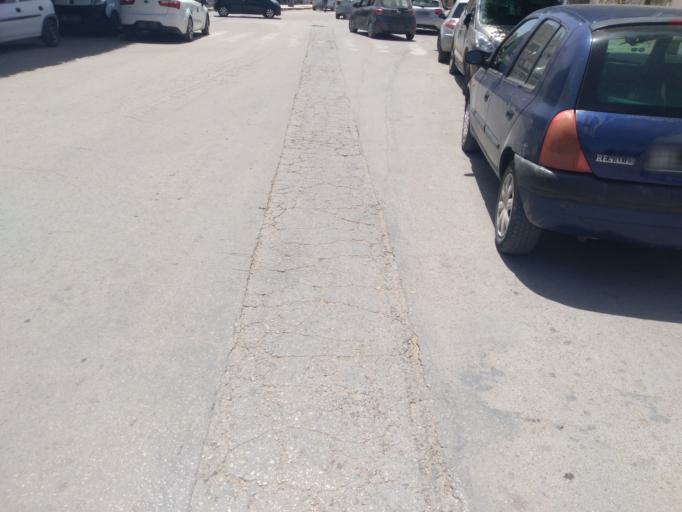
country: TN
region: Al Qayrawan
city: Kairouan
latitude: 35.6732
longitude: 10.1025
